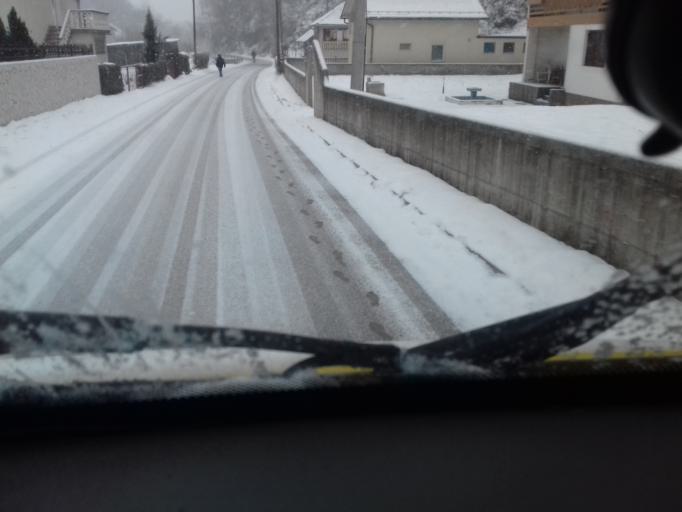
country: BA
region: Federation of Bosnia and Herzegovina
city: Zeljezno Polje
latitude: 44.3331
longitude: 17.9064
